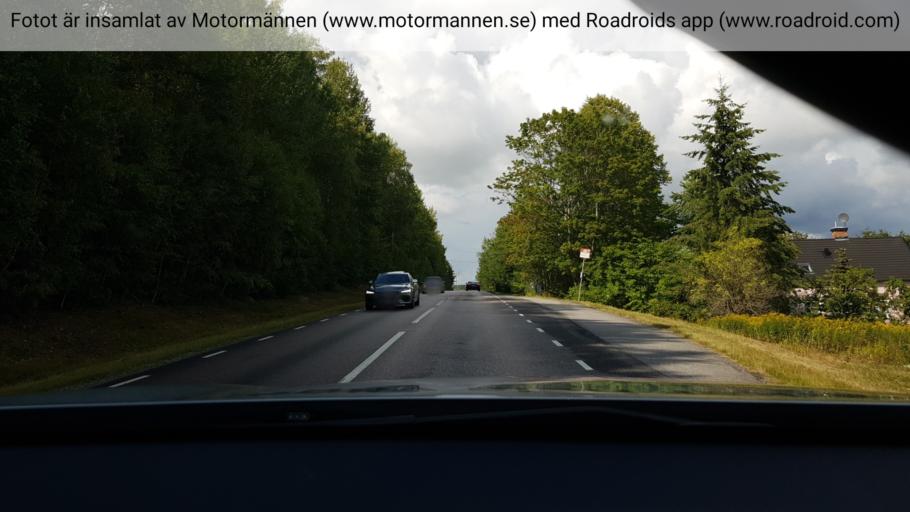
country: SE
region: Stockholm
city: Stenhamra
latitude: 59.3655
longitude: 17.6133
